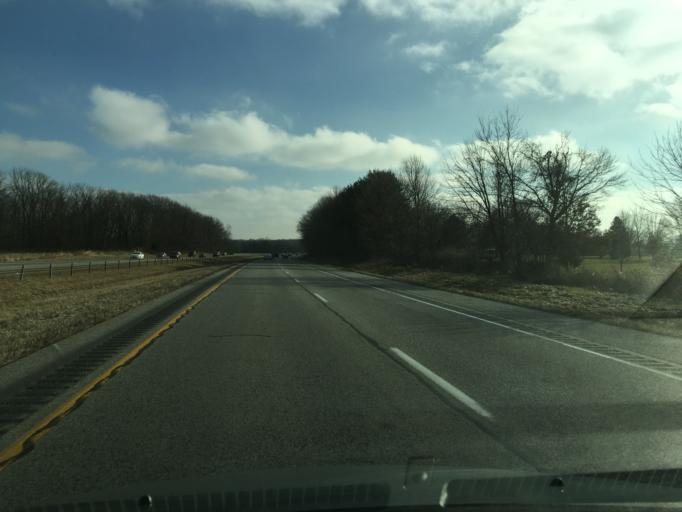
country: US
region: Indiana
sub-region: Decatur County
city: Saint Paul
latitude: 39.4002
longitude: -85.5536
